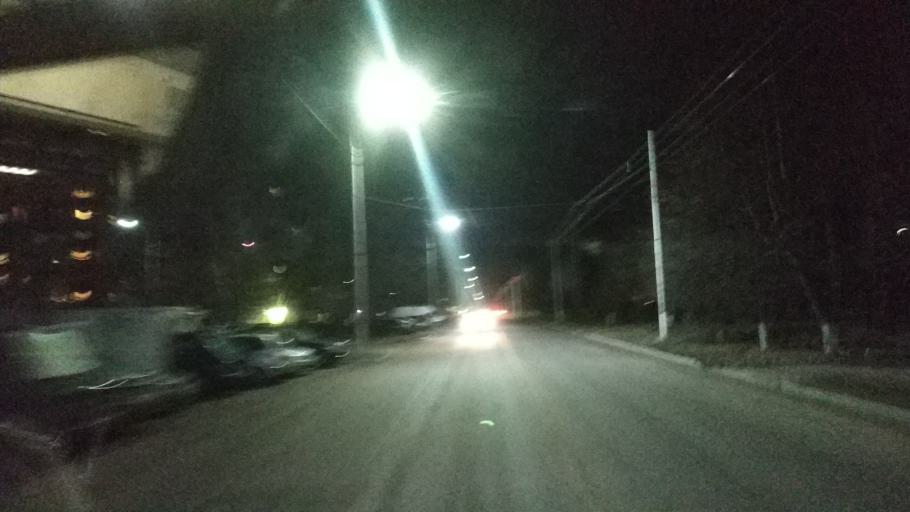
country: RU
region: Moskovskaya
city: Dubrovitsy
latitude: 55.4300
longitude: 37.4922
